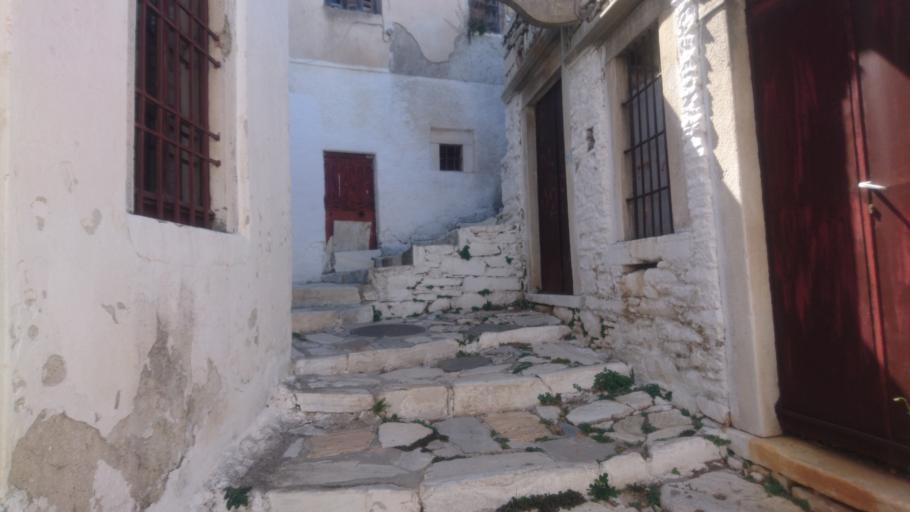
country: GR
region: South Aegean
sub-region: Nomos Kykladon
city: Filotion
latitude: 37.0726
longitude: 25.5215
